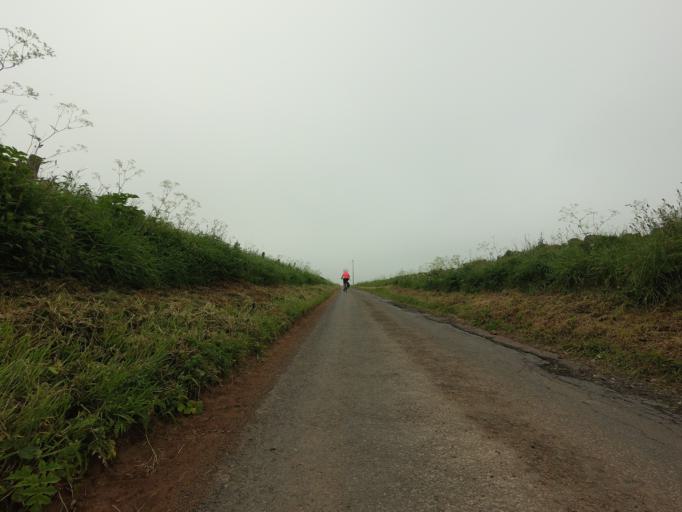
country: GB
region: Scotland
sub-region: Perth and Kinross
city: Abernethy
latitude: 56.2584
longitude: -3.3187
